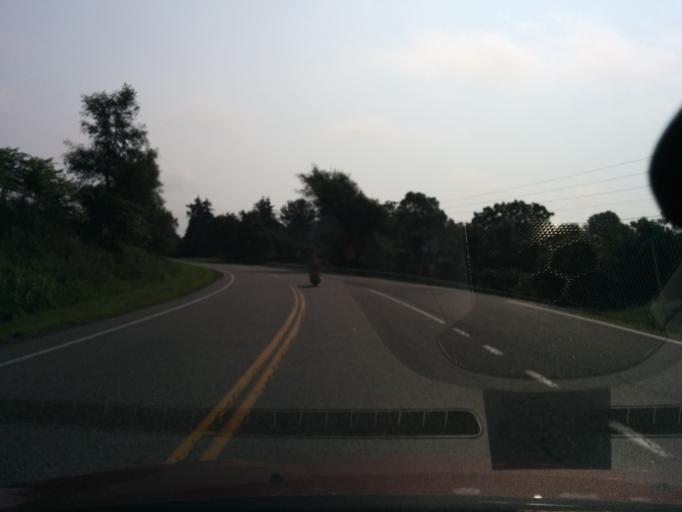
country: US
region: Virginia
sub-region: City of Lexington
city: Lexington
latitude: 37.7561
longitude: -79.4716
